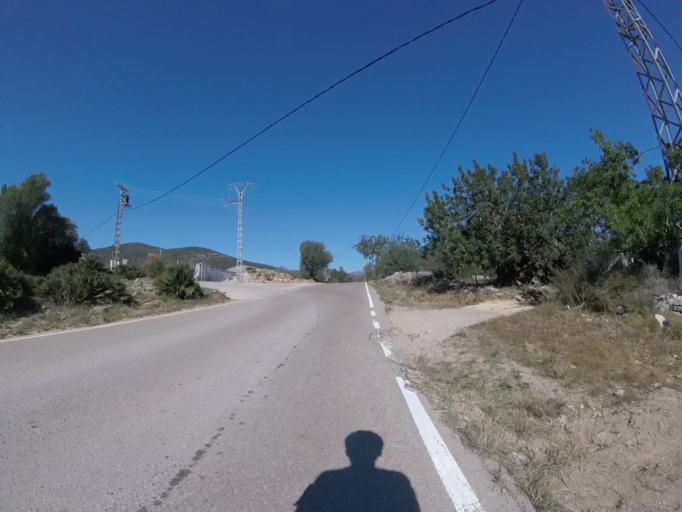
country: ES
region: Valencia
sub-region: Provincia de Castello
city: Santa Magdalena de Pulpis
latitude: 40.3616
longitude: 0.2823
